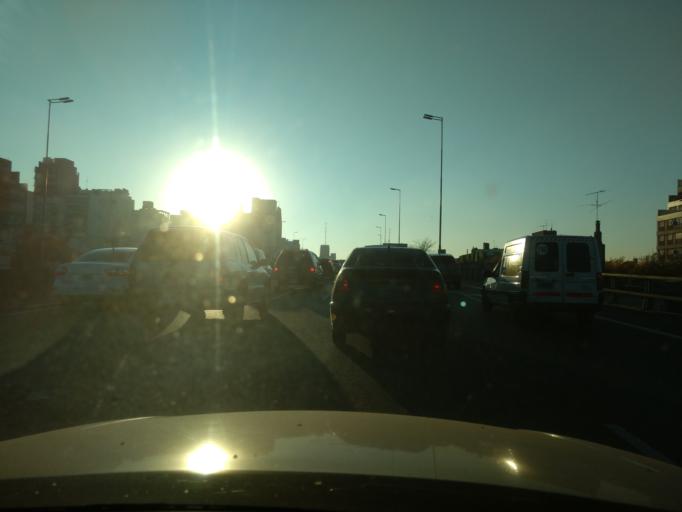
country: AR
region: Buenos Aires F.D.
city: Villa Santa Rita
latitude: -34.6303
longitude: -58.4360
